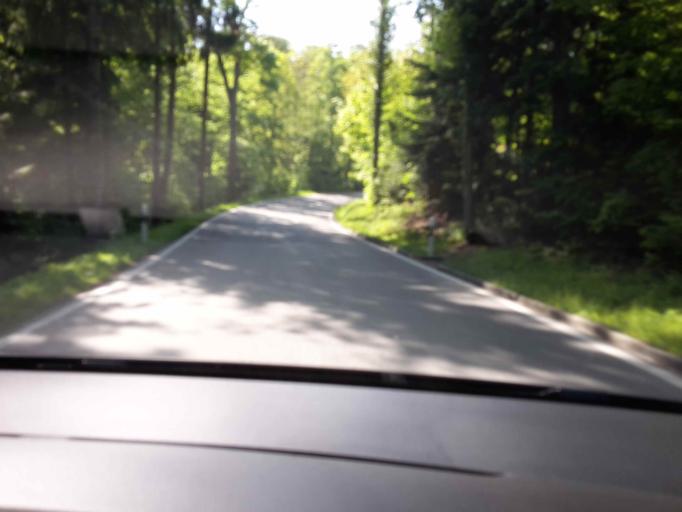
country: CH
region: Bern
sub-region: Thun District
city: Thun
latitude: 46.7551
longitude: 7.6431
